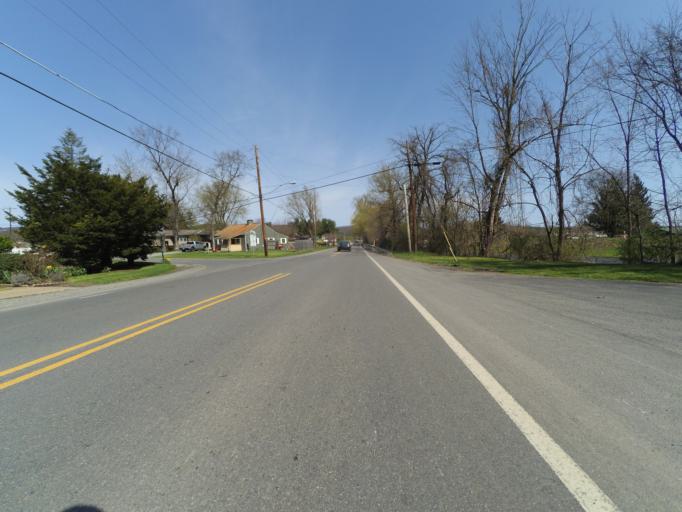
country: US
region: Pennsylvania
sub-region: Clinton County
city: Mill Hall
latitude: 41.1102
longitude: -77.4876
